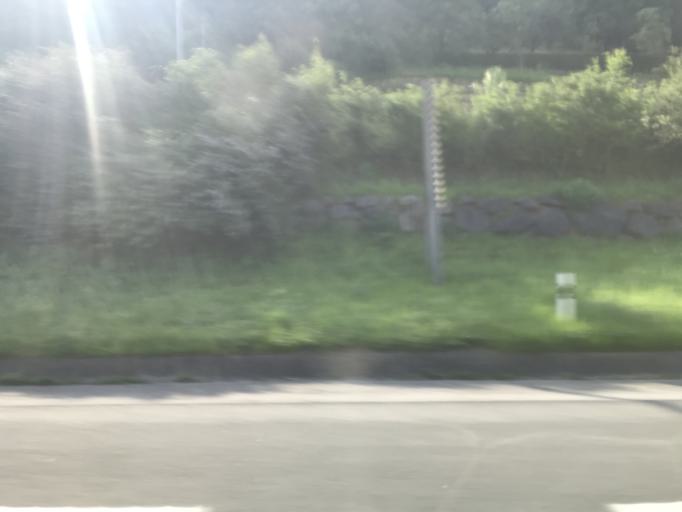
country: ES
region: Basque Country
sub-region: Provincia de Guipuzcoa
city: Aduna
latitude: 43.2002
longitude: -2.0389
